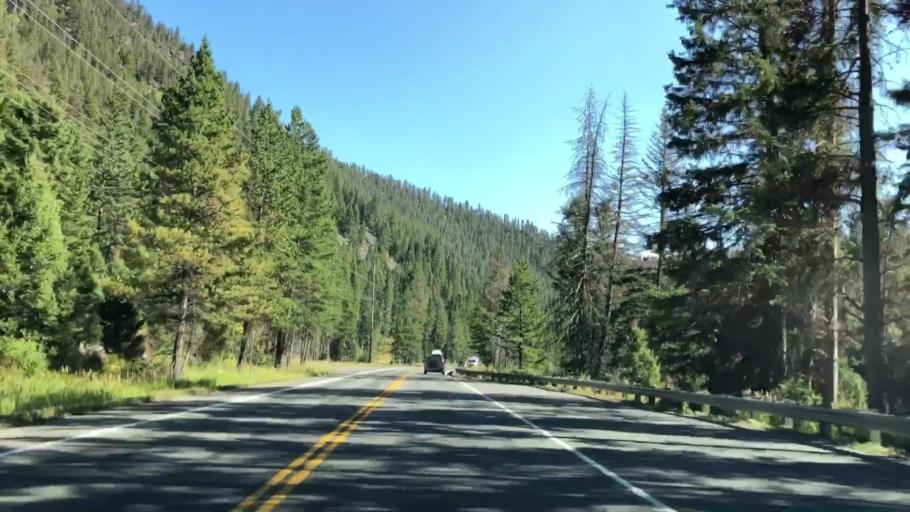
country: US
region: Montana
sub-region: Gallatin County
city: Big Sky
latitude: 45.3637
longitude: -111.1732
